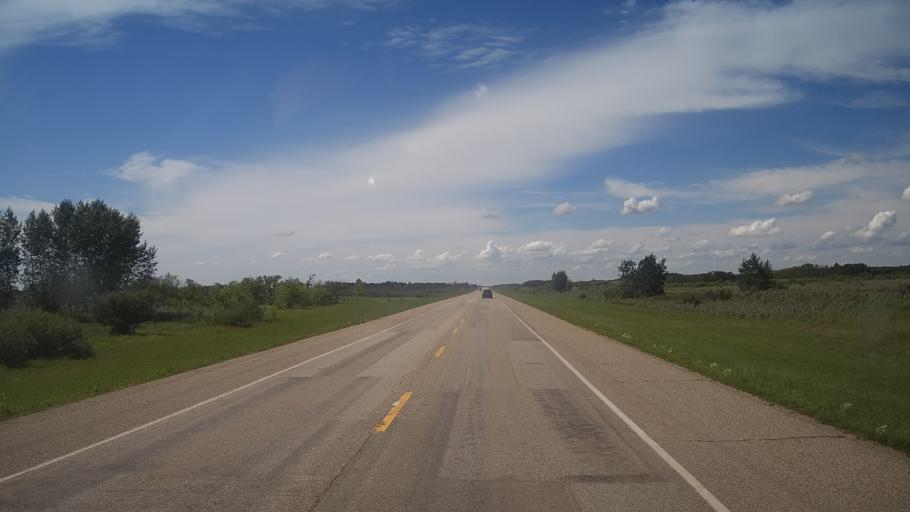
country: CA
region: Saskatchewan
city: Yorkton
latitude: 51.0582
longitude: -102.1993
